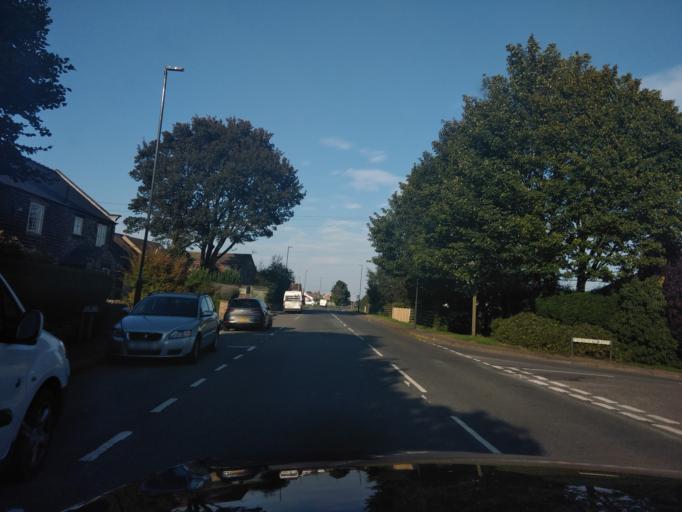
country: GB
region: England
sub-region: Derbyshire
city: Dronfield
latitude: 53.3038
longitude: -1.4991
